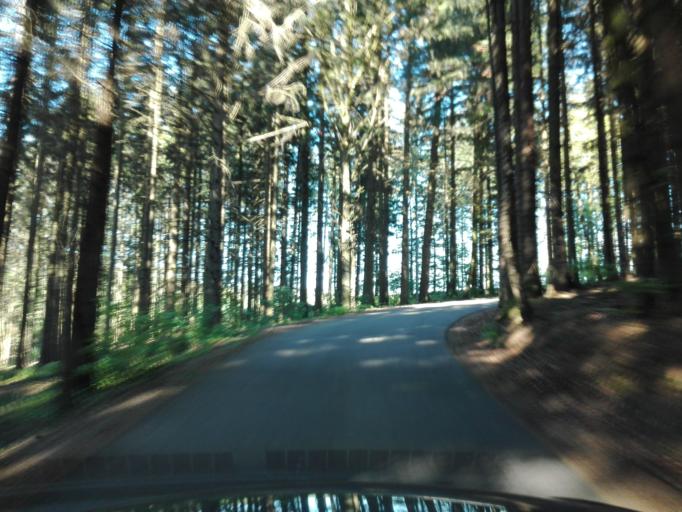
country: AT
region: Upper Austria
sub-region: Politischer Bezirk Rohrbach
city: Pfarrkirchen im Muehlkreis
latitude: 48.4688
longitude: 13.8311
